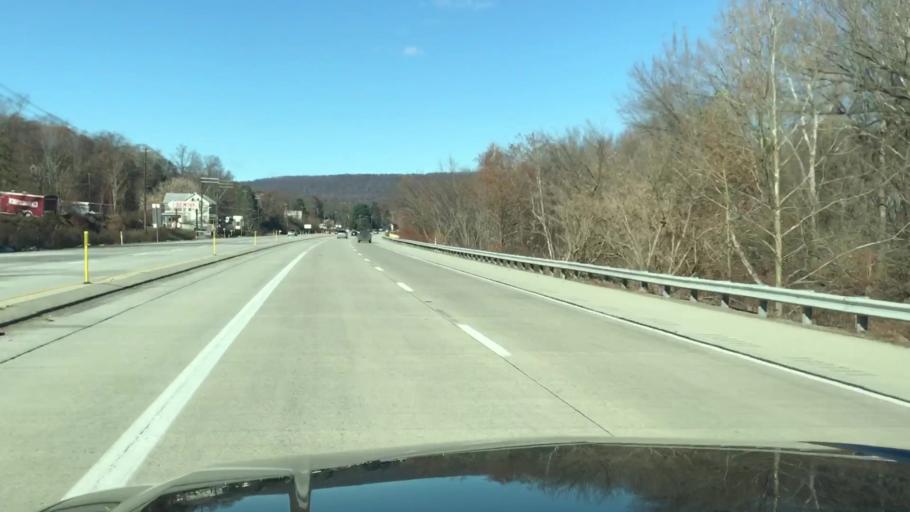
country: US
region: Pennsylvania
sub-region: Dauphin County
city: Millersburg
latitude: 40.4956
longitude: -76.9663
